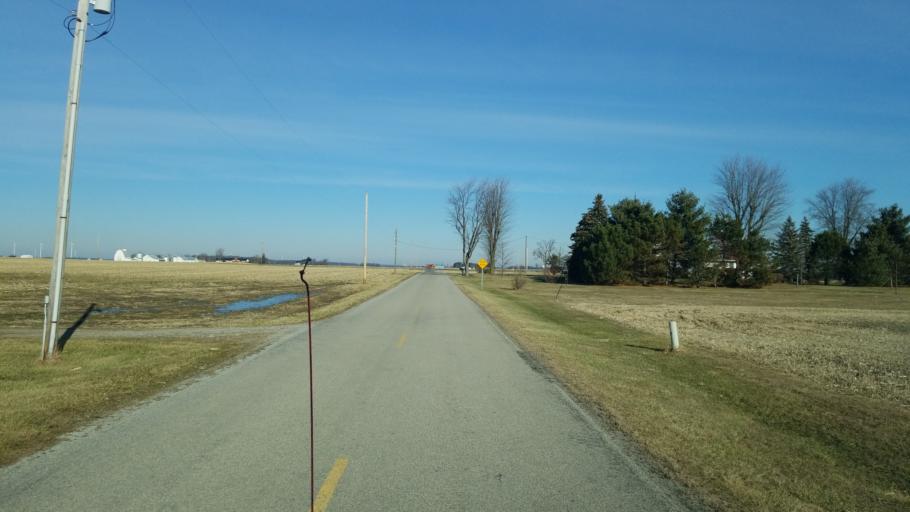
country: US
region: Ohio
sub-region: Hardin County
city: Kenton
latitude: 40.7295
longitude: -83.6913
